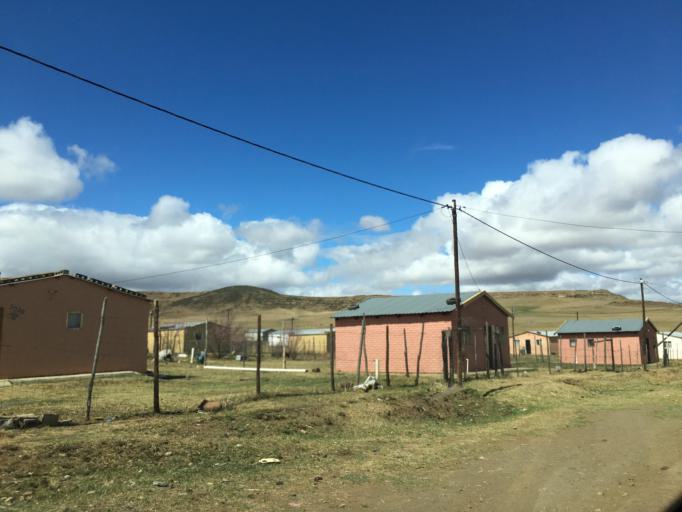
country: ZA
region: Eastern Cape
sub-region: Chris Hani District Municipality
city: Cala
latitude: -31.5422
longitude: 27.6983
